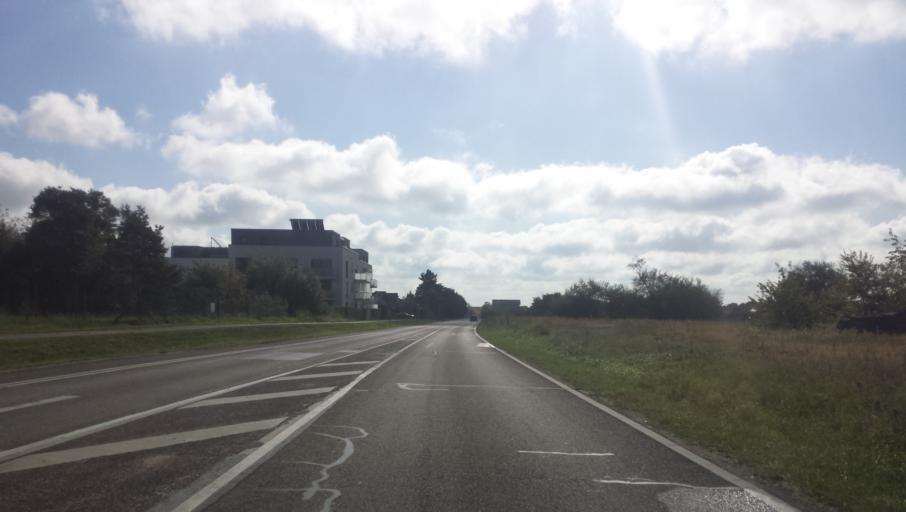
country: DE
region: Baden-Wuerttemberg
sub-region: Karlsruhe Region
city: Waghausel
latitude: 49.2380
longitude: 8.5086
